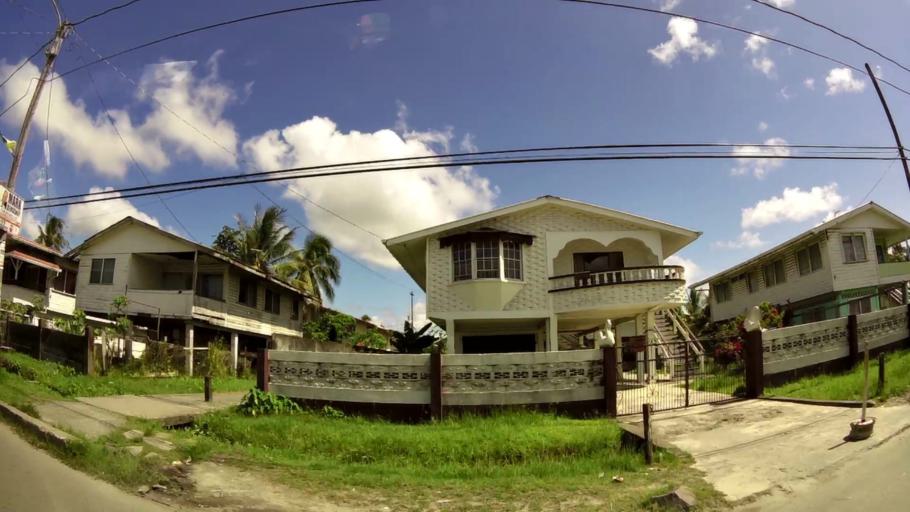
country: GY
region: Demerara-Mahaica
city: Georgetown
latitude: 6.7820
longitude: -58.1244
